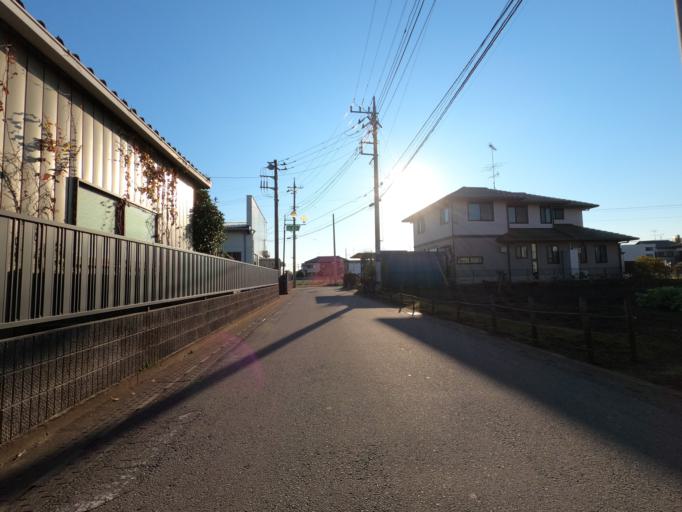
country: JP
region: Ibaraki
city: Moriya
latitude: 35.9381
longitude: 139.9980
